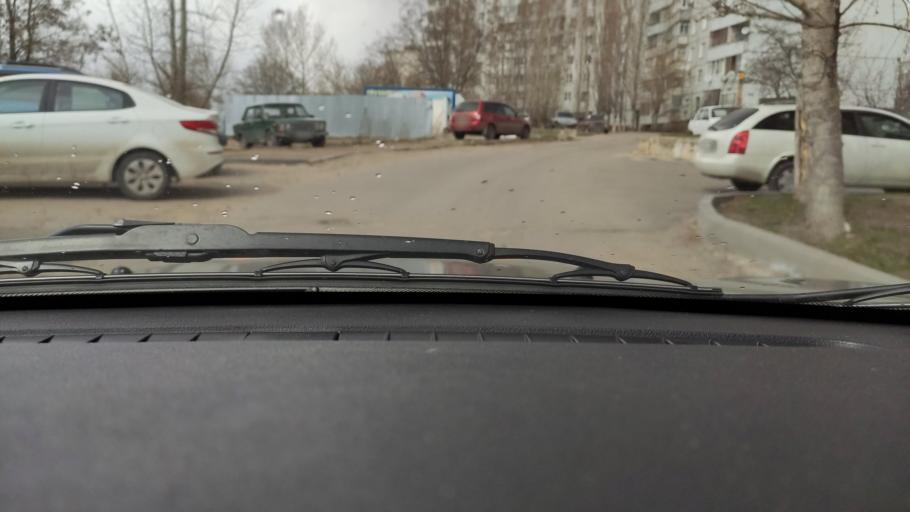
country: RU
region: Voronezj
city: Shilovo
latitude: 51.5582
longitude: 39.1151
